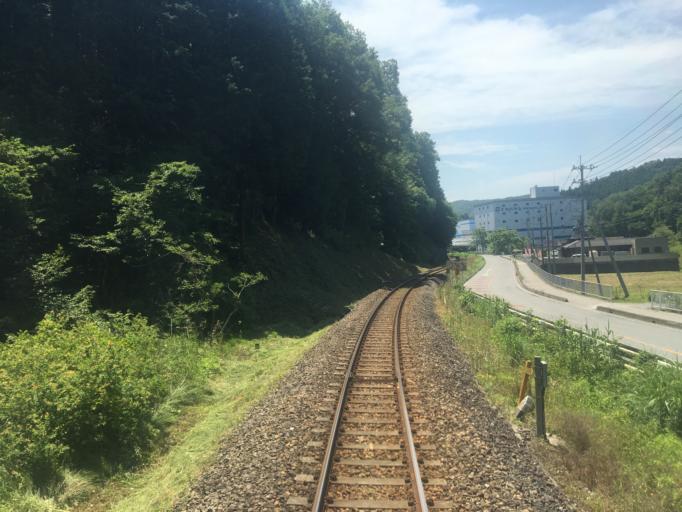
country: JP
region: Saitama
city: Ogawa
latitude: 36.0308
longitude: 139.2634
